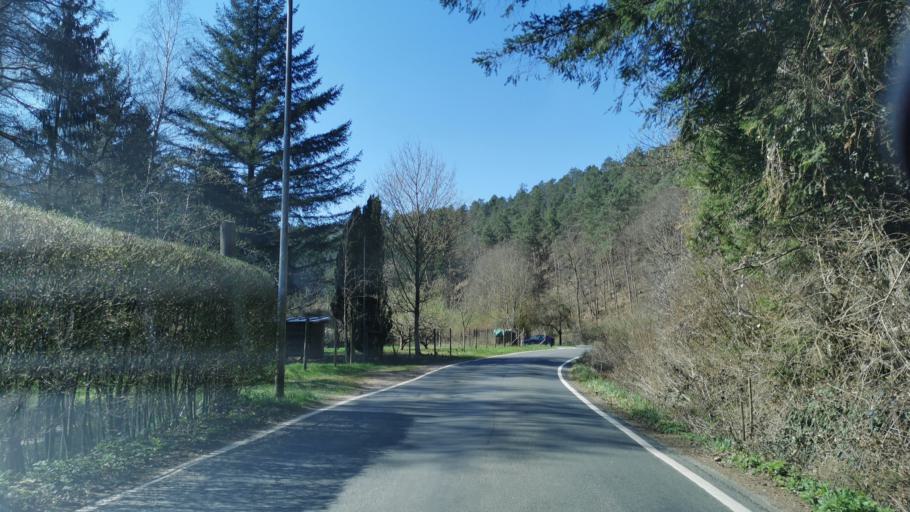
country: DE
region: Rheinland-Pfalz
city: Trier
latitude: 49.7830
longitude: 6.6571
